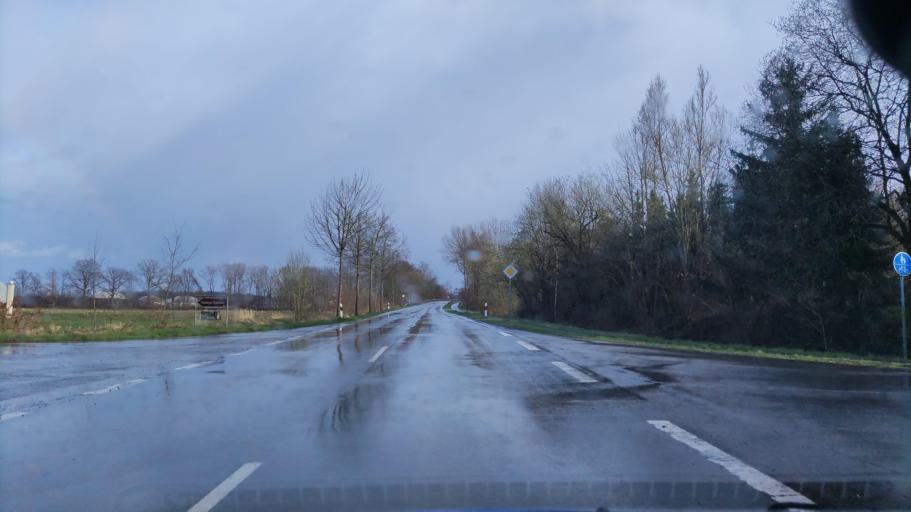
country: DE
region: Lower Saxony
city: Eschede
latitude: 52.7450
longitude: 10.2289
